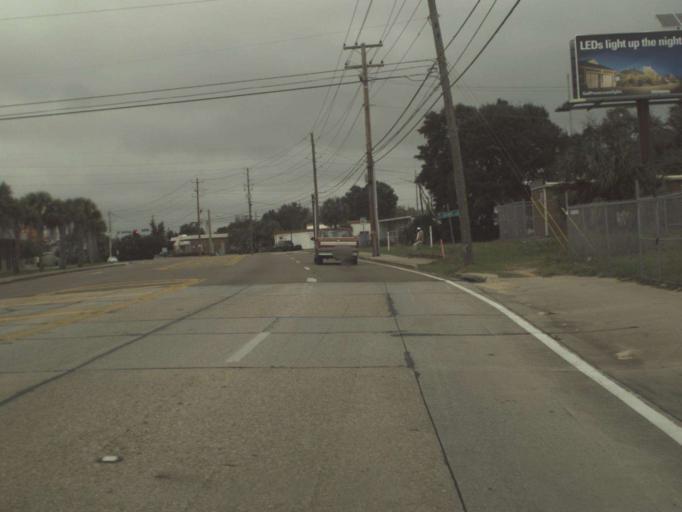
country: US
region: Florida
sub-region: Escambia County
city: Goulding
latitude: 30.4371
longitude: -87.2209
